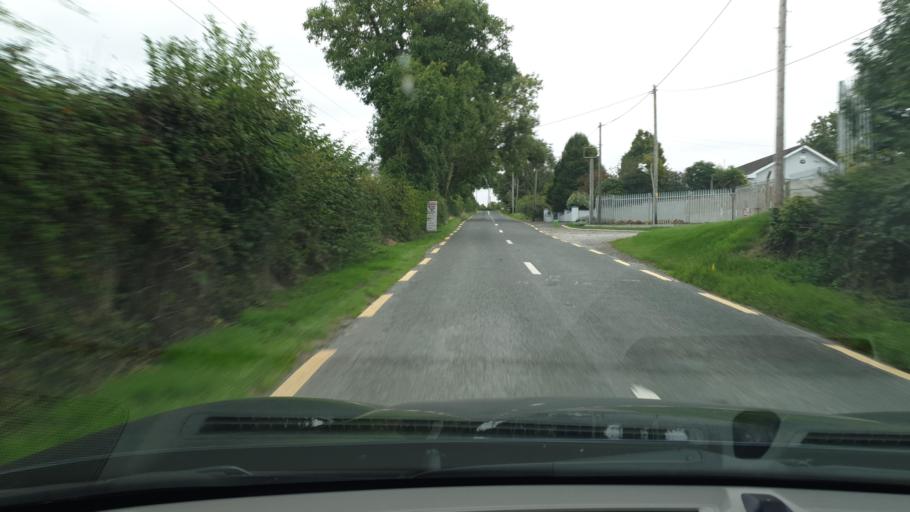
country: IE
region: Leinster
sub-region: Kildare
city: Kilcock
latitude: 53.4541
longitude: -6.6392
